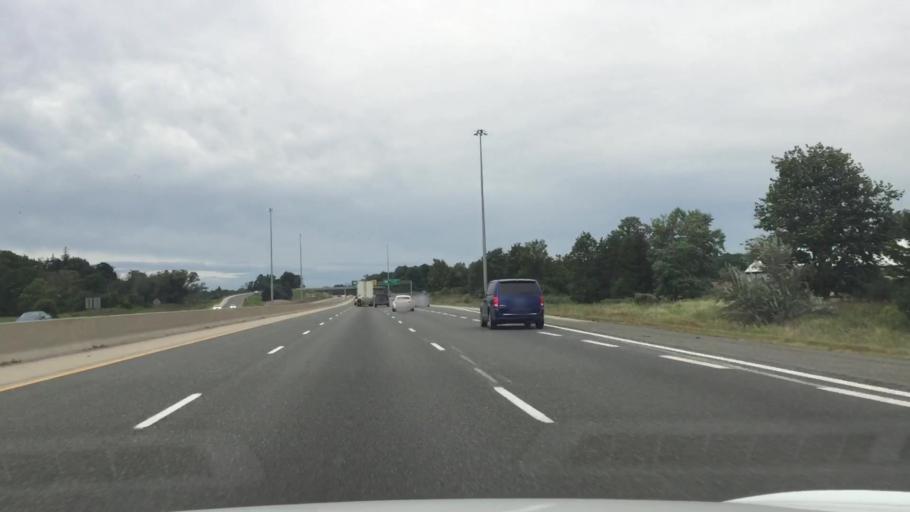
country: CA
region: Ontario
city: London
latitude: 42.9099
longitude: -81.2291
